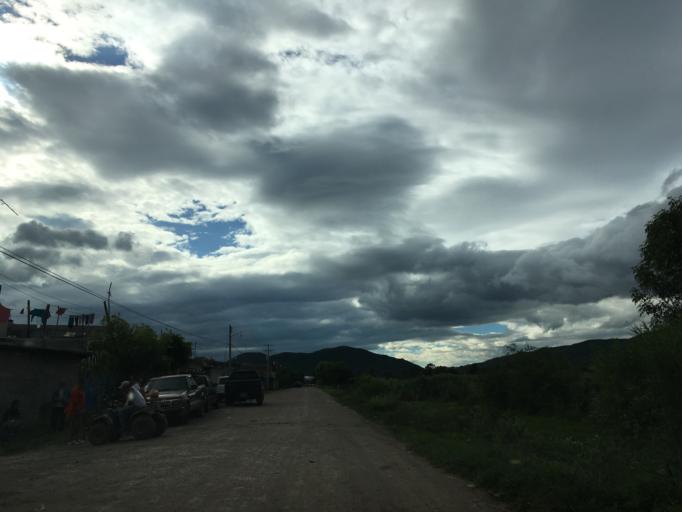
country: MX
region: Guanajuato
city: Iramuco
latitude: 19.9676
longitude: -100.9453
